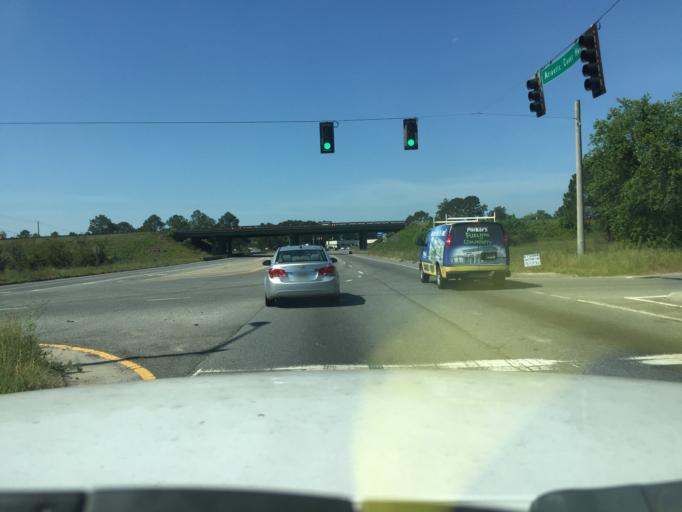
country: US
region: Georgia
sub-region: Chatham County
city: Georgetown
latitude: 32.0011
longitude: -81.2474
